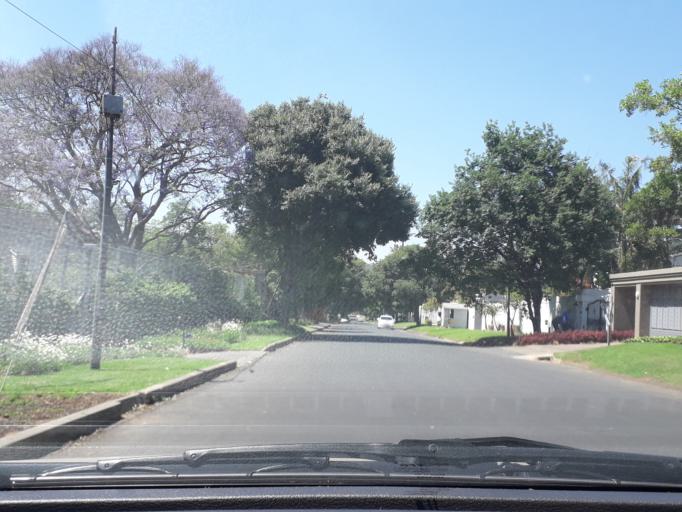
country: ZA
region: Gauteng
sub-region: City of Johannesburg Metropolitan Municipality
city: Johannesburg
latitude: -26.1514
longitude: 28.0690
